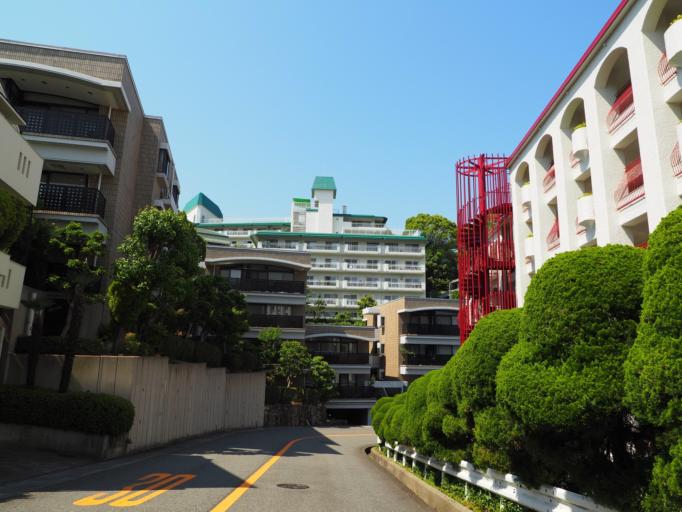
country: JP
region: Hyogo
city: Ashiya
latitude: 34.7408
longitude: 135.3044
